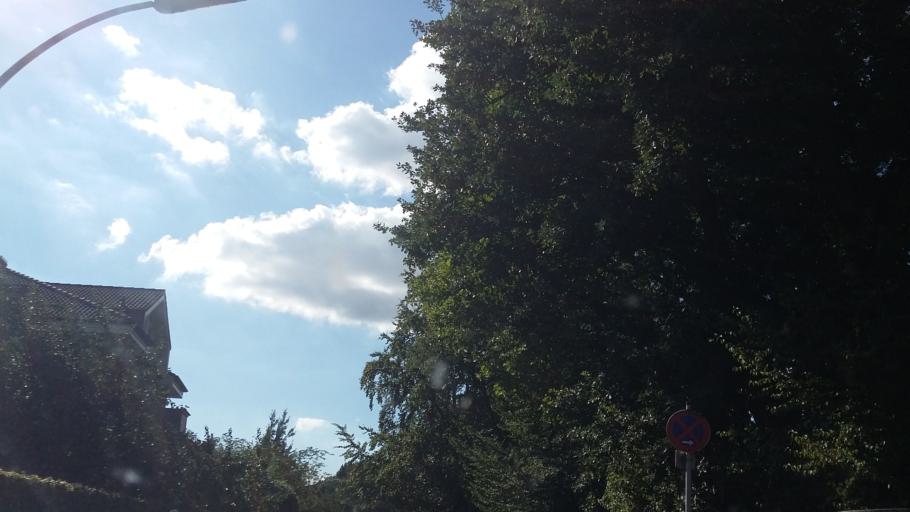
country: DE
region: Hamburg
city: Altona
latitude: 53.5504
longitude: 9.8836
